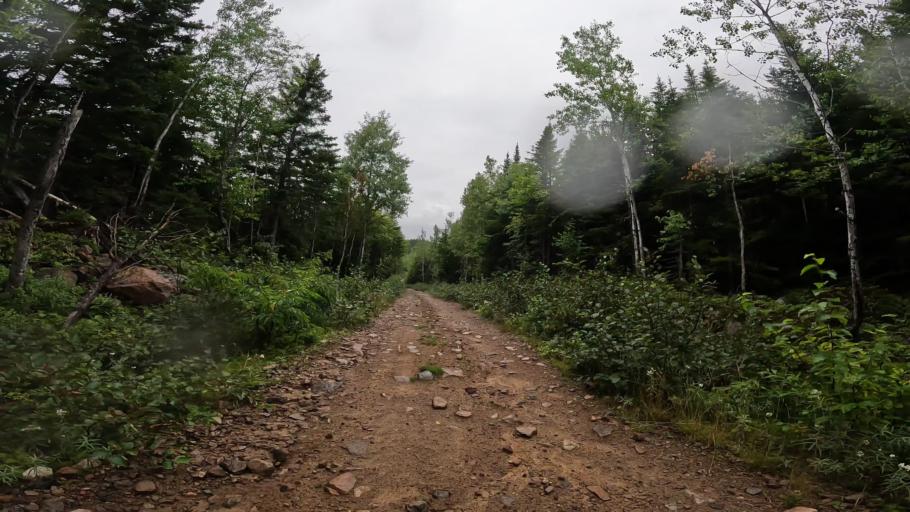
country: CA
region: Quebec
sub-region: Capitale-Nationale
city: La Malbaie
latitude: 47.8081
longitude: -70.4815
